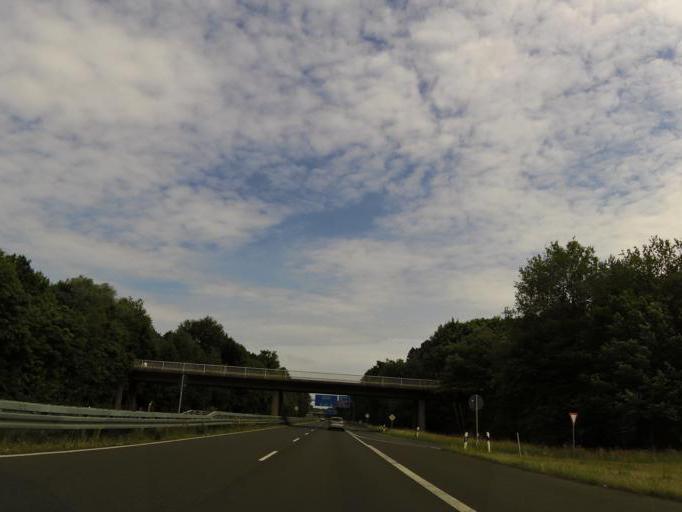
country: DE
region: Hesse
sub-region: Regierungsbezirk Darmstadt
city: Neu Isenburg
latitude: 50.0756
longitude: 8.7171
